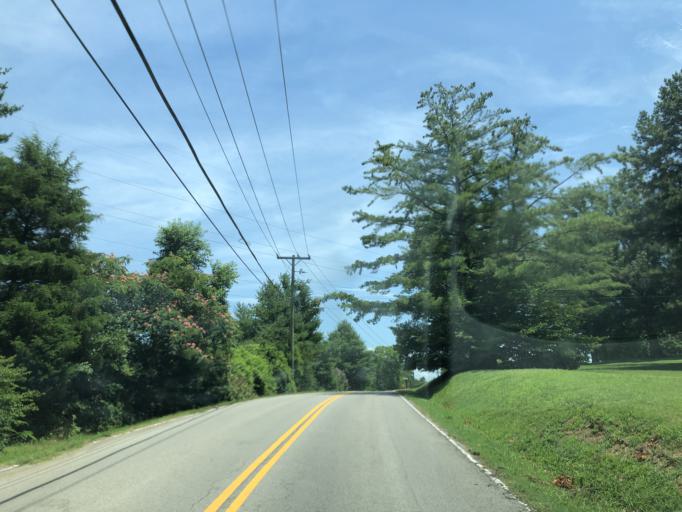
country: US
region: Tennessee
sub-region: Rutherford County
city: La Vergne
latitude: 36.0344
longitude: -86.6606
